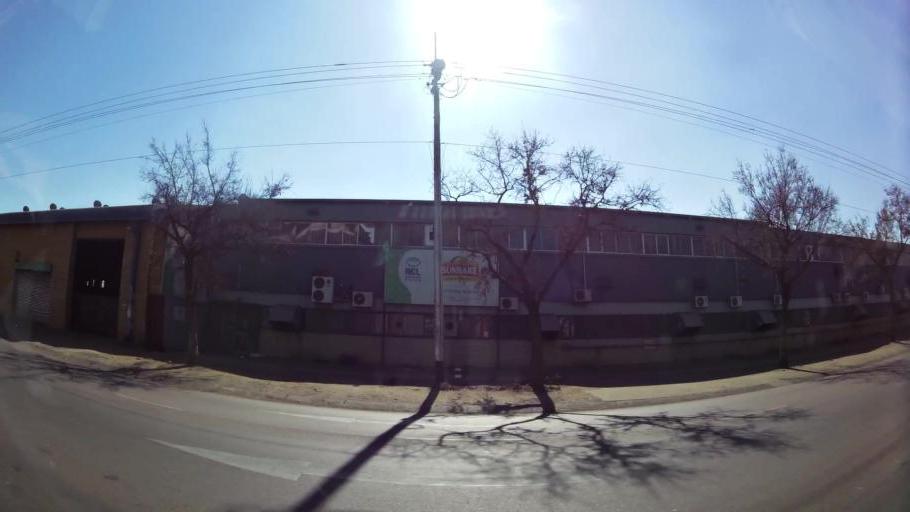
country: ZA
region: Gauteng
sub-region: City of Tshwane Metropolitan Municipality
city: Pretoria
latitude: -25.7550
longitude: 28.1559
